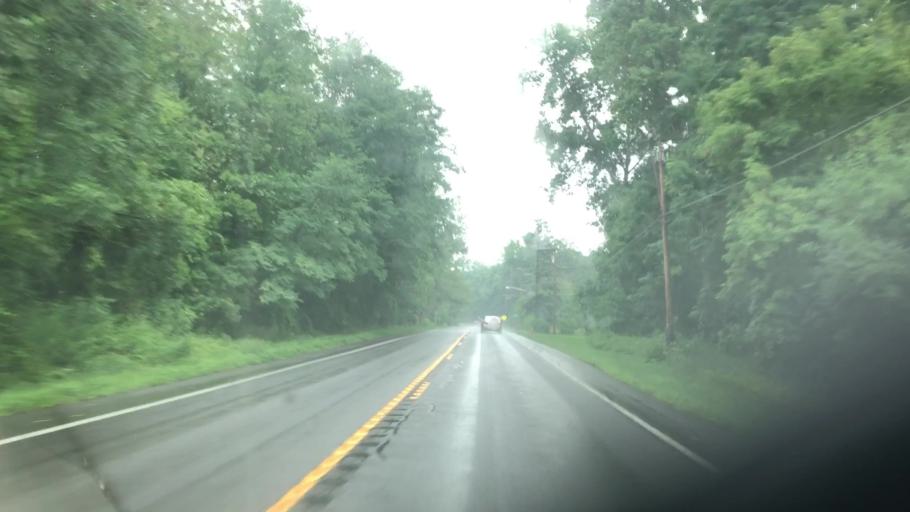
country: US
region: New York
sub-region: Monroe County
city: Fairport
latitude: 43.1295
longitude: -77.4238
